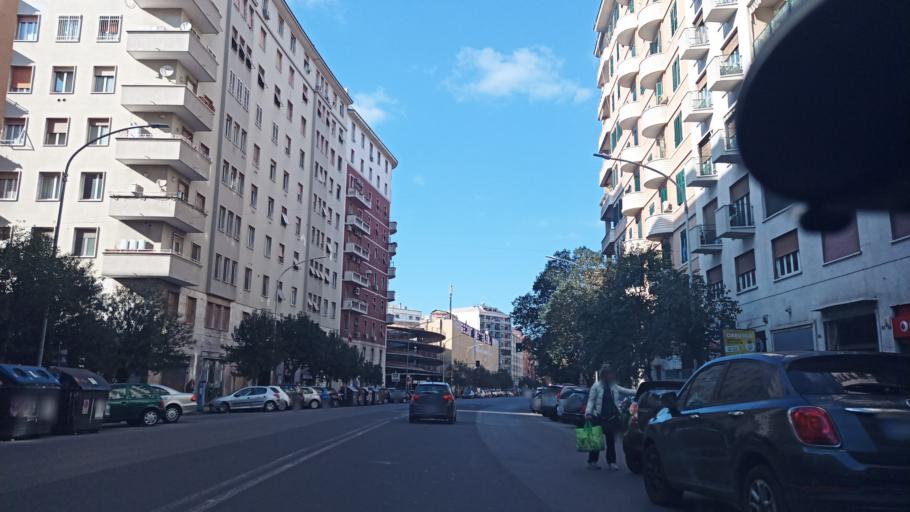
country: IT
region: Latium
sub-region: Citta metropolitana di Roma Capitale
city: Rome
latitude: 41.8813
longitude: 12.5081
